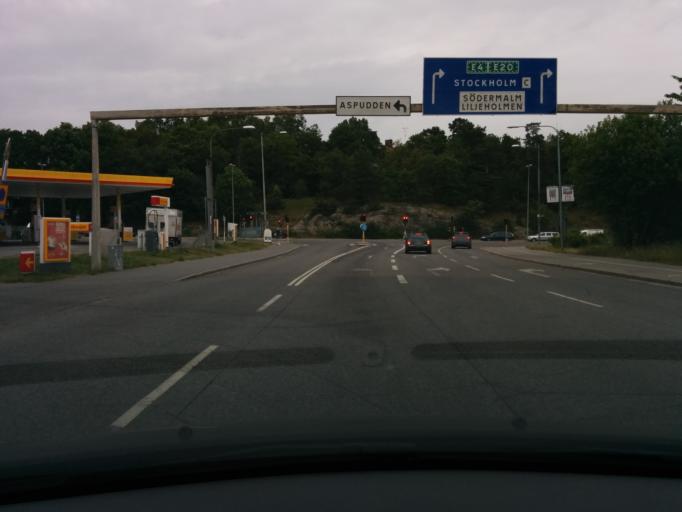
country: SE
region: Stockholm
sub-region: Stockholms Kommun
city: Arsta
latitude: 59.3050
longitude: 18.0100
